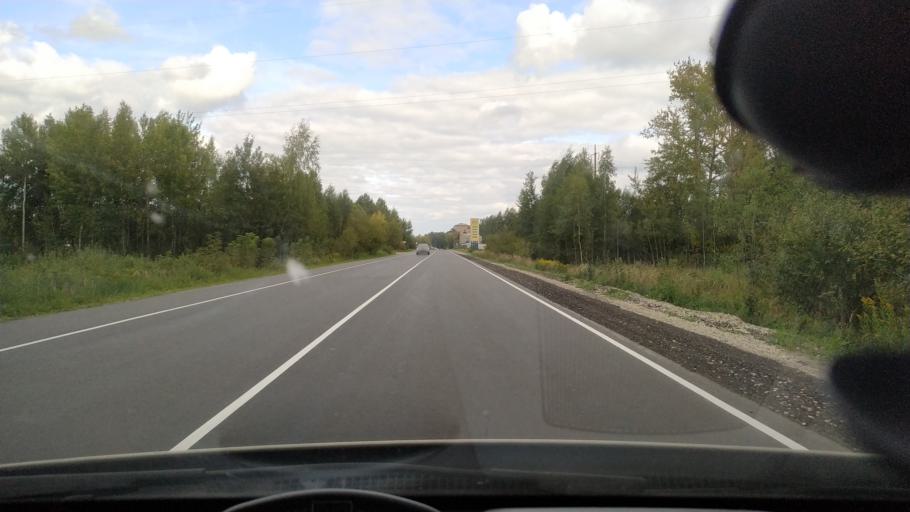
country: RU
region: Moskovskaya
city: Kabanovo
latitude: 55.7375
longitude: 38.9316
